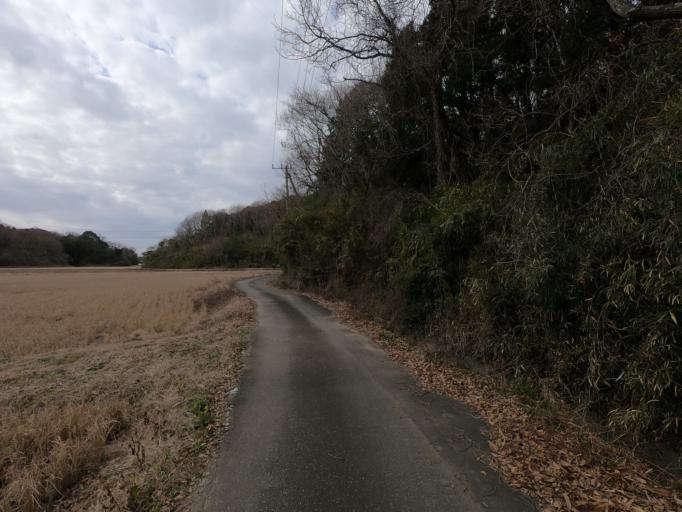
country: JP
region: Ibaraki
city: Inashiki
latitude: 36.0602
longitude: 140.4471
